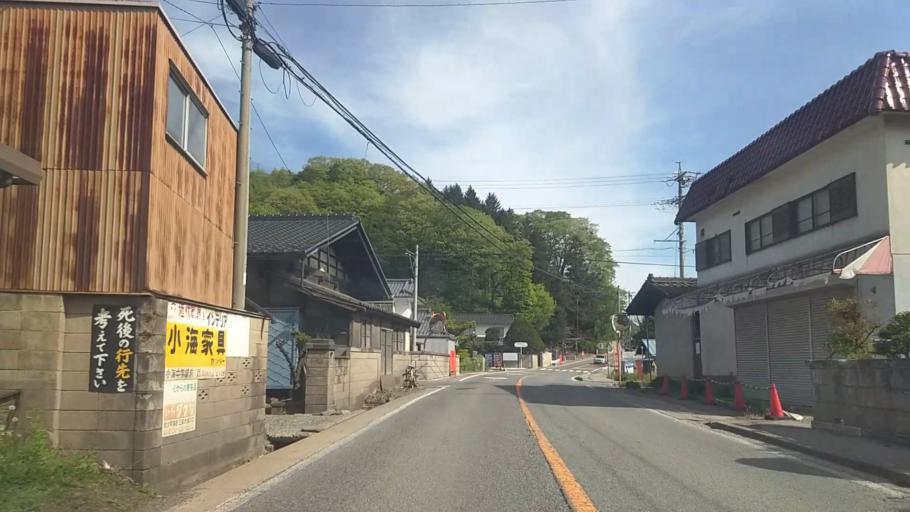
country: JP
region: Nagano
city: Saku
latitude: 36.0393
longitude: 138.4718
